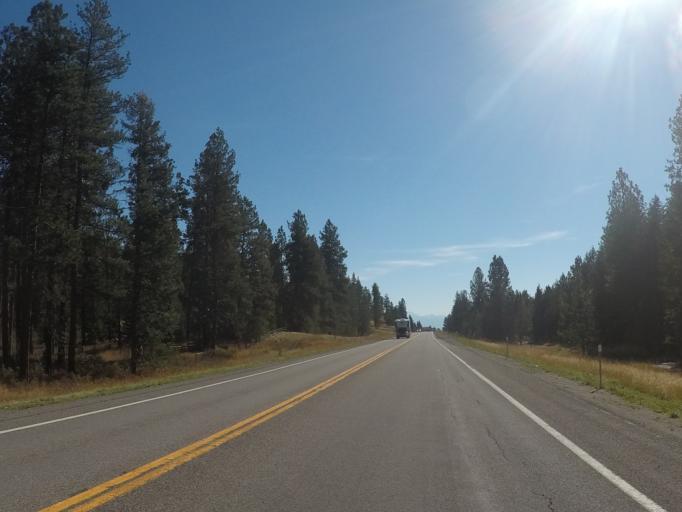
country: US
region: Montana
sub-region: Lake County
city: Polson
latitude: 47.7663
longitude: -114.2392
